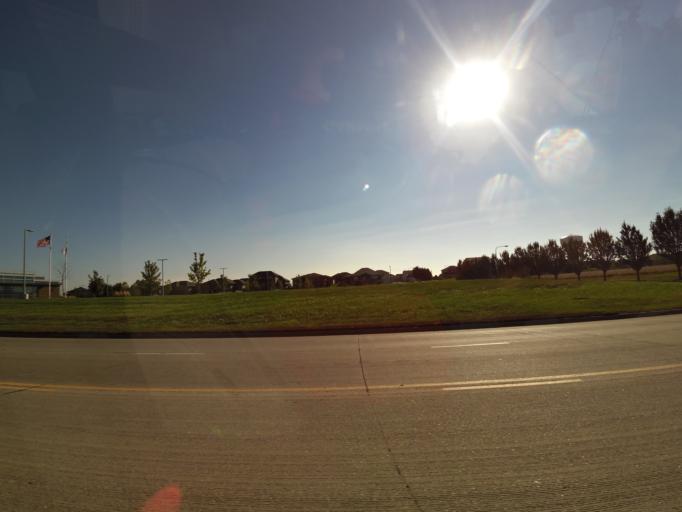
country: US
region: Nebraska
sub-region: Sarpy County
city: Gretna
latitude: 41.1289
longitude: -96.2529
